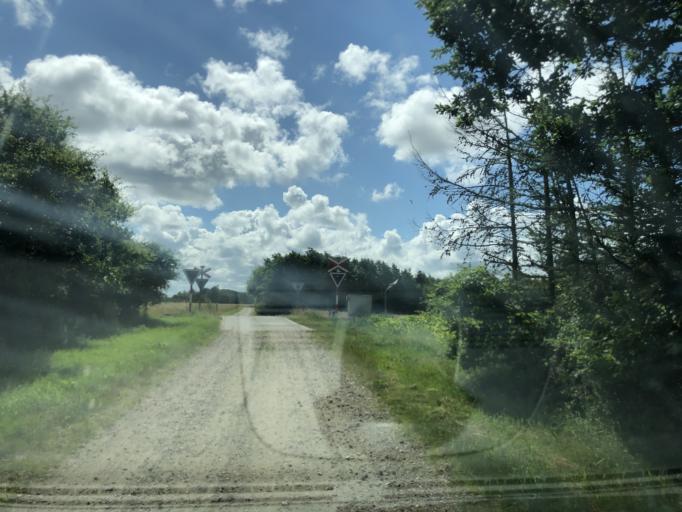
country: DK
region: Central Jutland
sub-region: Holstebro Kommune
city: Ulfborg
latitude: 56.3584
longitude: 8.3685
